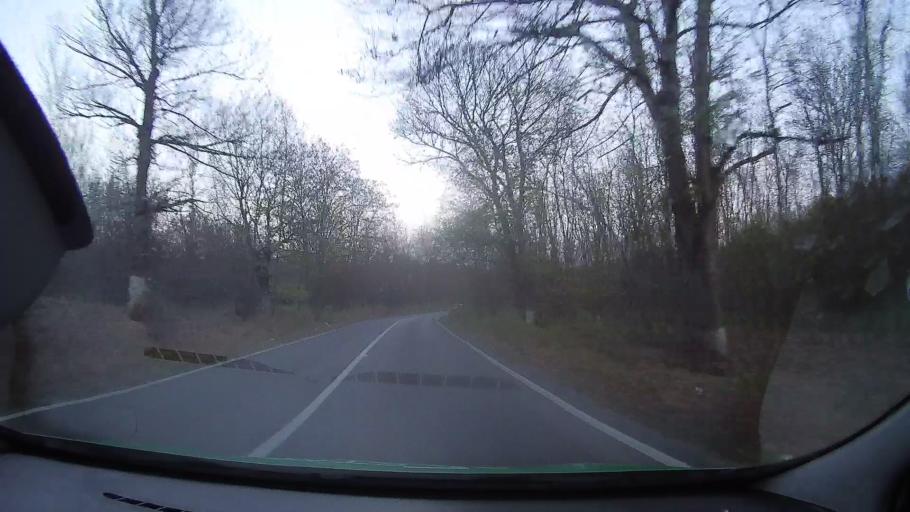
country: RO
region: Constanta
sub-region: Comuna Baneasa
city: Baneasa
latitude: 44.0873
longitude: 27.6623
